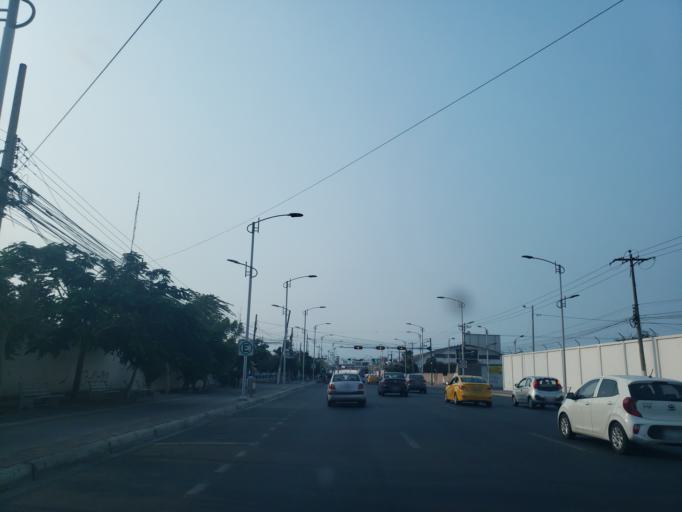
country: EC
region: Manabi
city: Manta
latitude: -0.9649
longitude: -80.7052
